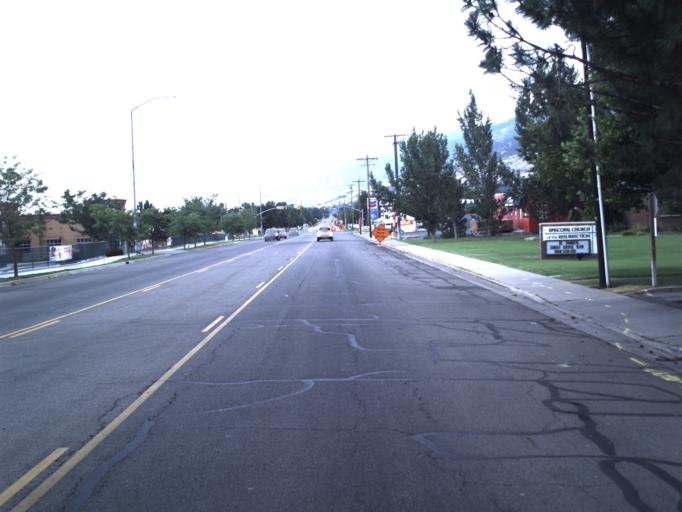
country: US
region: Utah
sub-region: Davis County
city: Centerville
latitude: 40.9045
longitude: -111.8790
